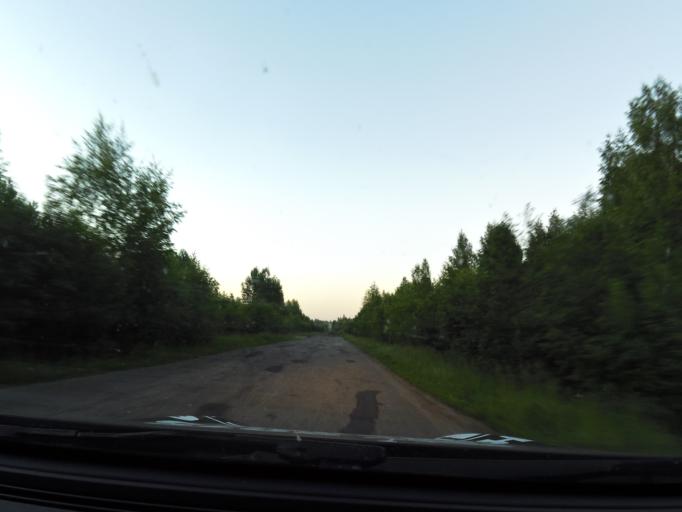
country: RU
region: Kostroma
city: Buy
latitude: 58.4124
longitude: 41.2513
